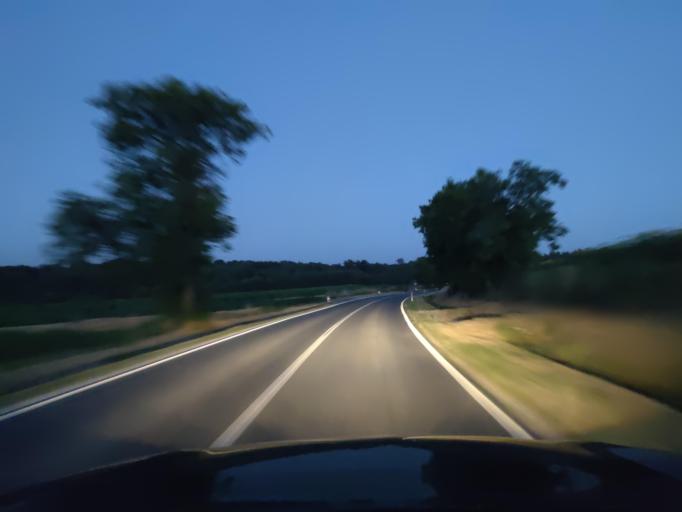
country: HR
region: Medimurska
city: Vratisinec
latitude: 46.4613
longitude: 16.4283
